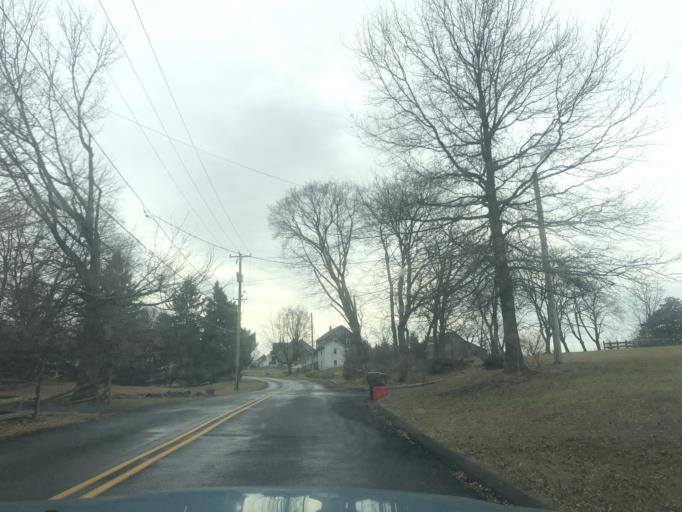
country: US
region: Pennsylvania
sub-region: Montgomery County
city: Harleysville
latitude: 40.2658
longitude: -75.4077
